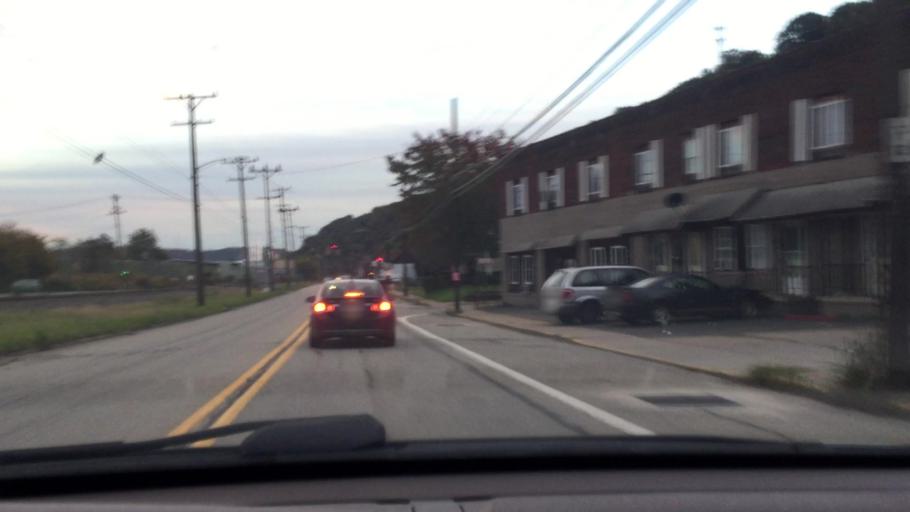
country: US
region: Pennsylvania
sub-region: Westmoreland County
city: Arnold
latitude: 40.5780
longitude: -79.7786
